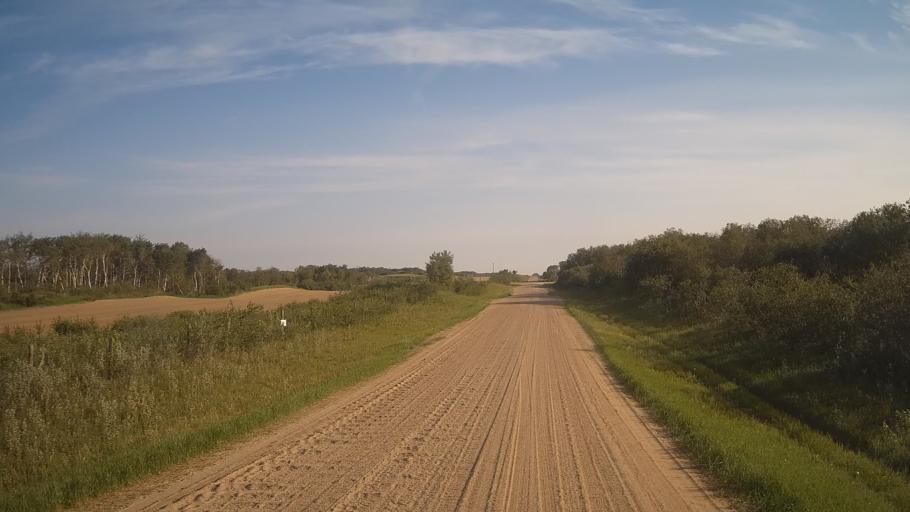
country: CA
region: Saskatchewan
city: Saskatoon
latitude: 51.8499
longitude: -106.5239
